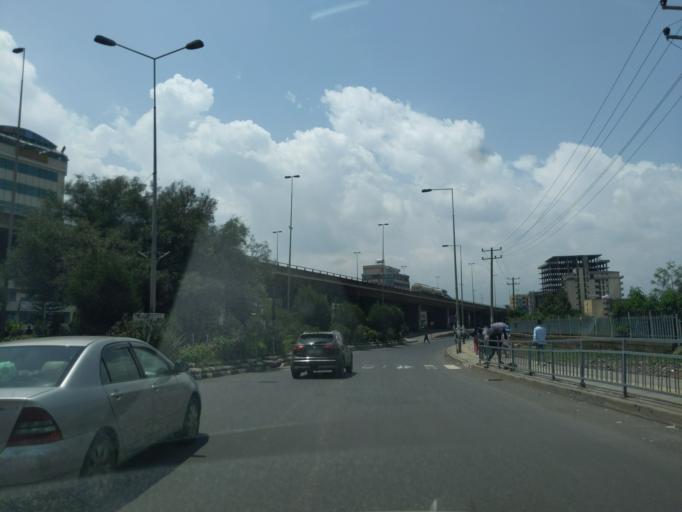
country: ET
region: Adis Abeba
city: Addis Ababa
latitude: 8.9876
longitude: 38.7921
